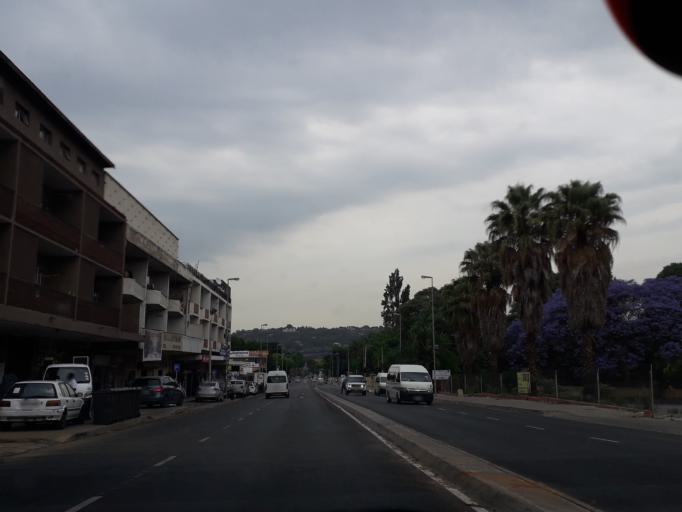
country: ZA
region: Gauteng
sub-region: City of Johannesburg Metropolitan Municipality
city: Johannesburg
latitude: -26.1472
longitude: 28.0867
